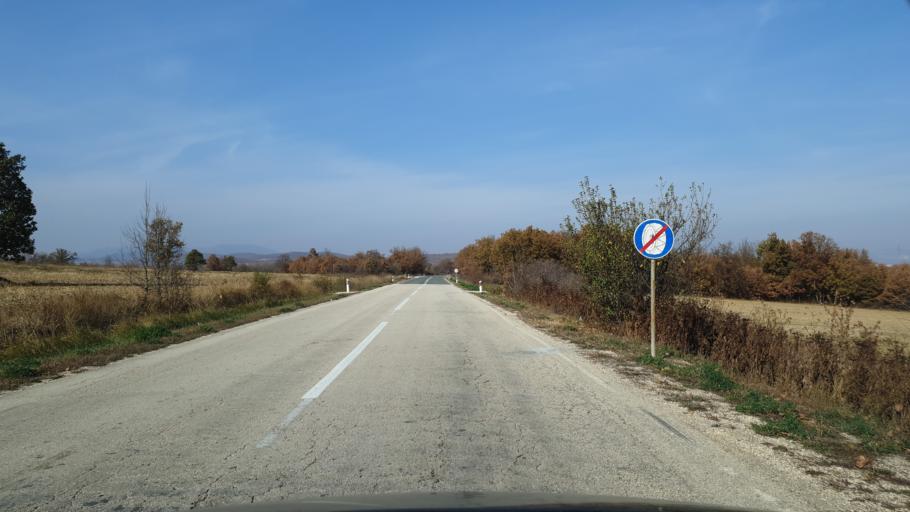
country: RS
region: Central Serbia
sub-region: Borski Okrug
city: Bor
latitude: 43.9976
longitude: 22.0714
